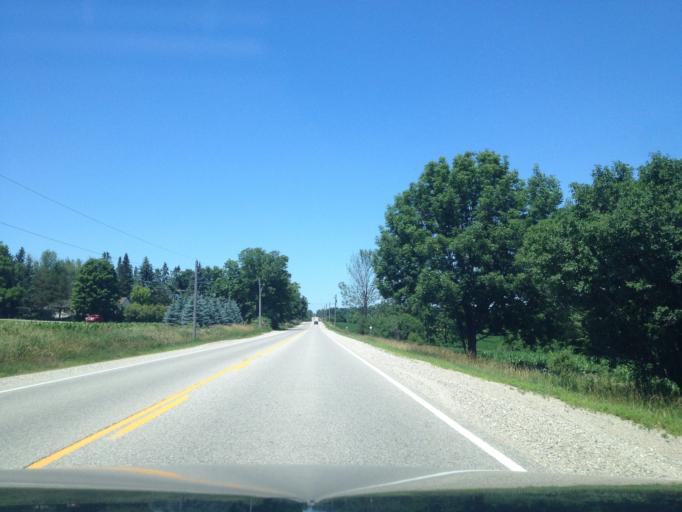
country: CA
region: Ontario
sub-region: Wellington County
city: Guelph
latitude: 43.6237
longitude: -80.2255
